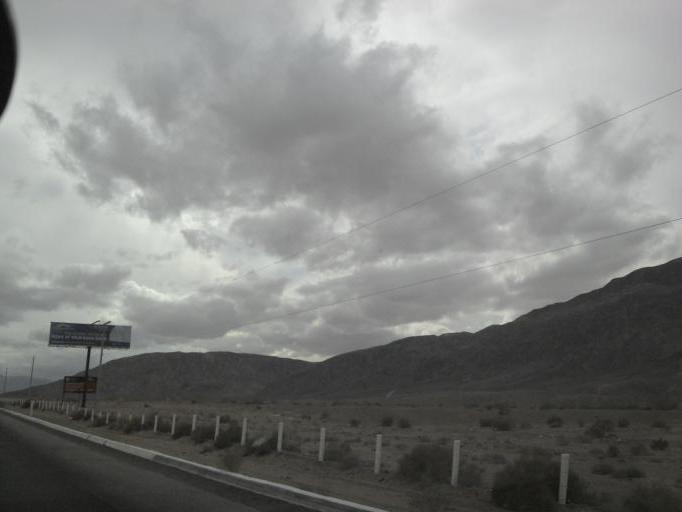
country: MX
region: Baja California
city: Progreso
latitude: 32.5916
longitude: -115.6945
